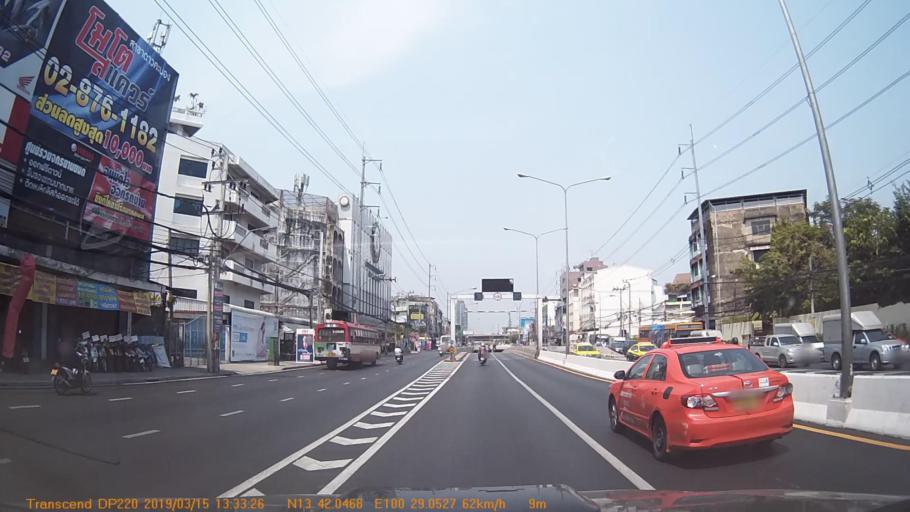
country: TH
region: Bangkok
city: Bang Kho Laem
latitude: 13.7010
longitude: 100.4843
